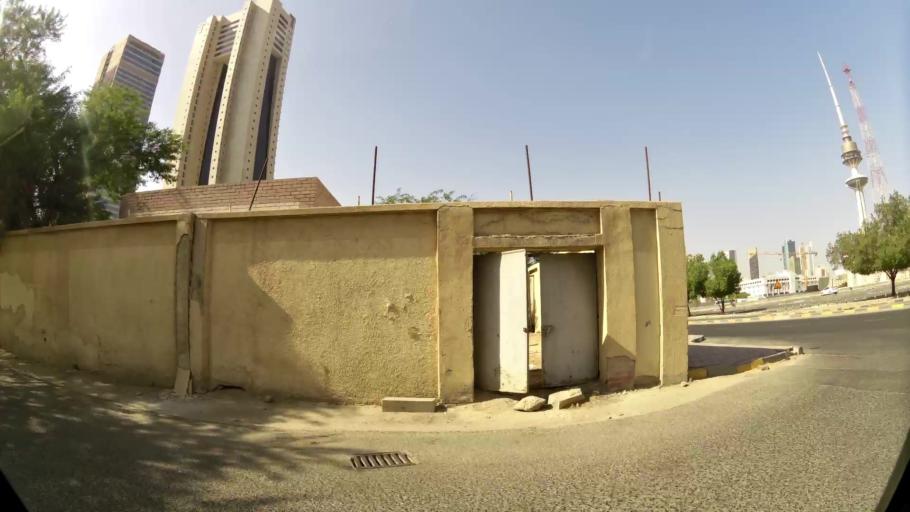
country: KW
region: Al Asimah
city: Kuwait City
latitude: 29.3653
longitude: 47.9816
